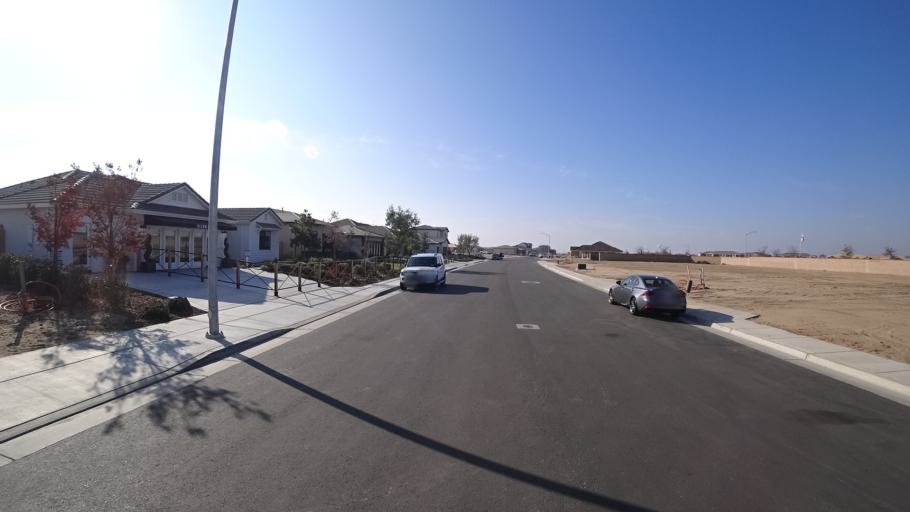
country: US
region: California
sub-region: Kern County
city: Rosedale
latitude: 35.3493
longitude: -119.1754
